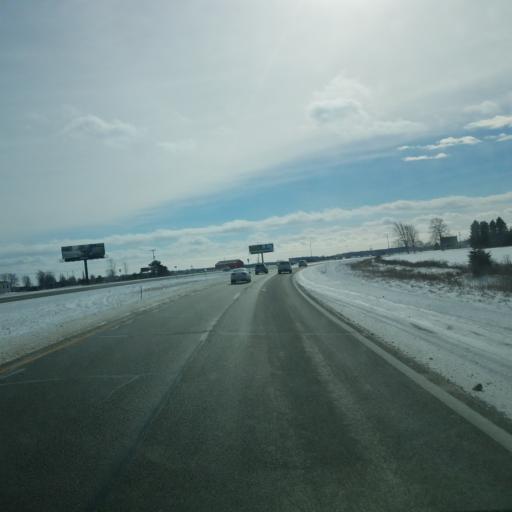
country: US
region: Michigan
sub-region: Gratiot County
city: Ithaca
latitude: 43.2691
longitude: -84.5643
